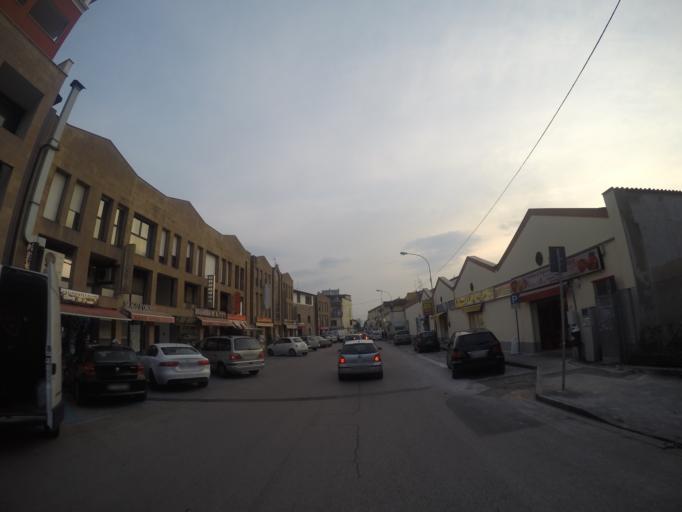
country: IT
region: Tuscany
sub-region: Provincia di Prato
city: Prato
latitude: 43.8846
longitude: 11.0902
